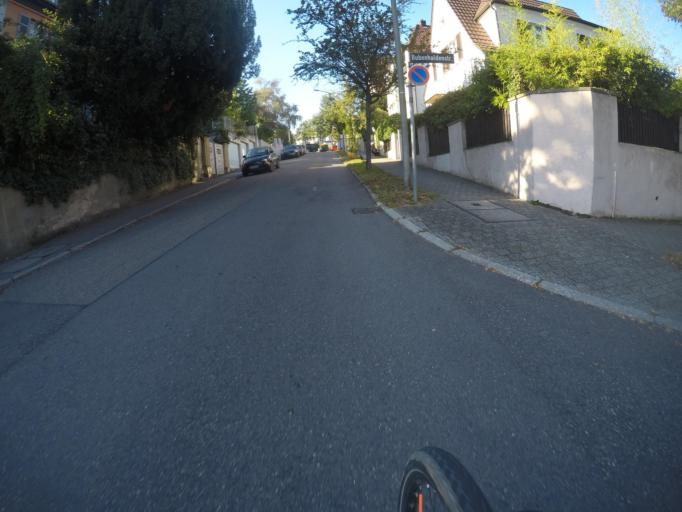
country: DE
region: Baden-Wuerttemberg
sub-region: Regierungsbezirk Stuttgart
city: Stuttgart Feuerbach
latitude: 48.8140
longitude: 9.1541
